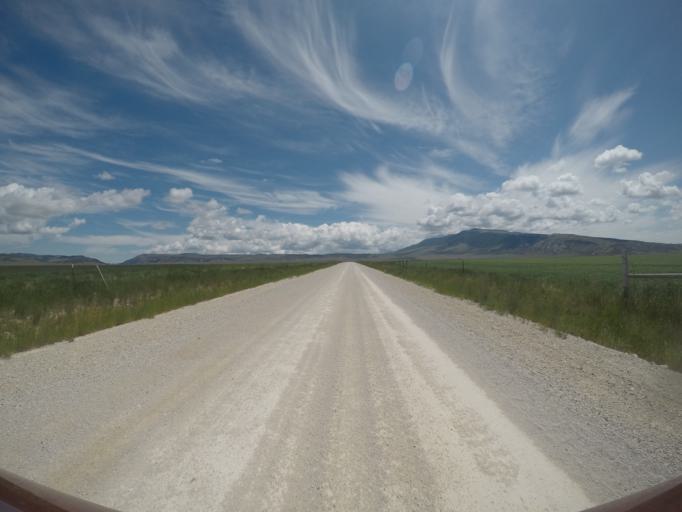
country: US
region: Montana
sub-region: Yellowstone County
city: Laurel
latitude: 45.2195
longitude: -108.7038
